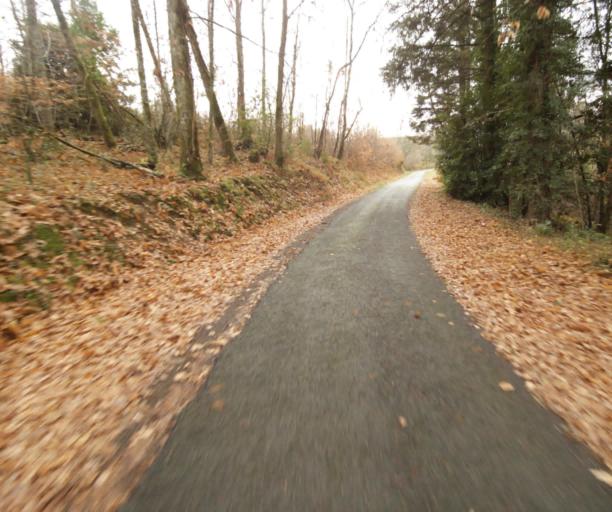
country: FR
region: Limousin
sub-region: Departement de la Correze
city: Saint-Mexant
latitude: 45.2760
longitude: 1.6413
